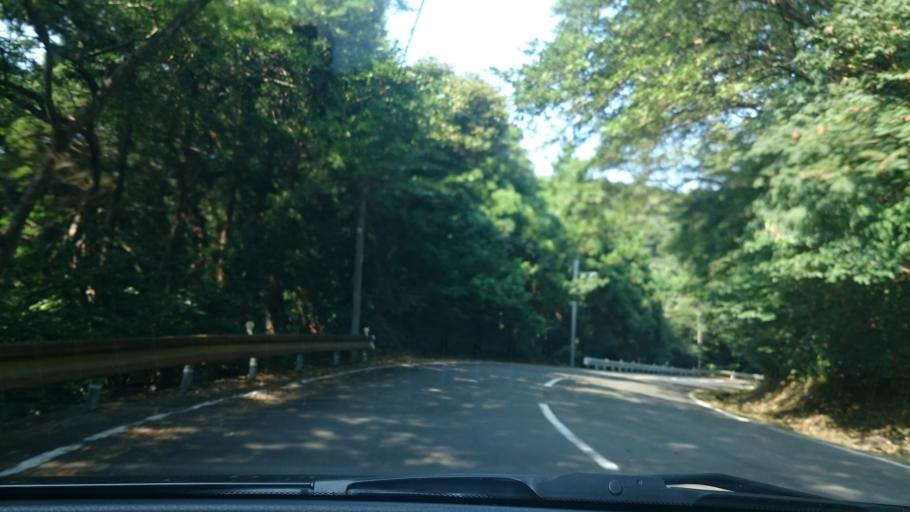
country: JP
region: Shizuoka
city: Heda
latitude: 34.9891
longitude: 138.7768
